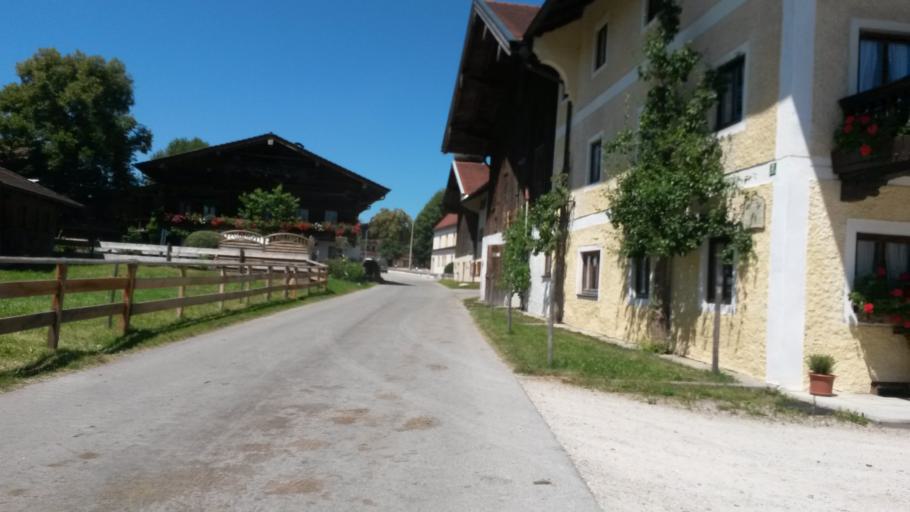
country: DE
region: Bavaria
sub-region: Upper Bavaria
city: Grassau
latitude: 47.7942
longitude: 12.4173
